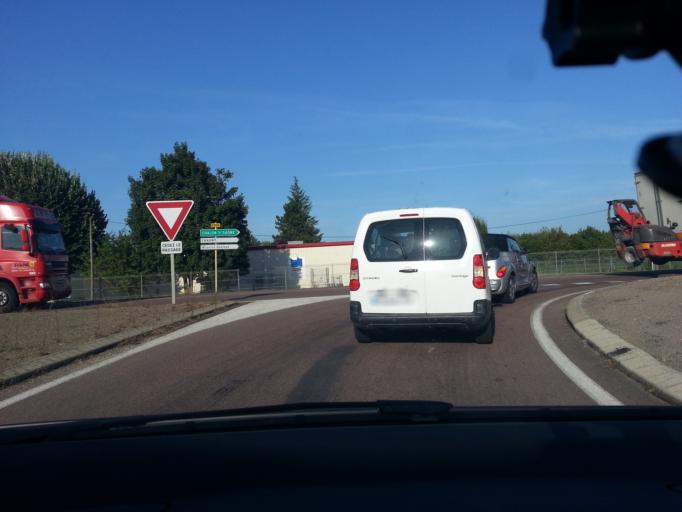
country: FR
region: Bourgogne
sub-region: Departement de la Cote-d'Or
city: Corpeau
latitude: 46.9285
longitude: 4.7417
